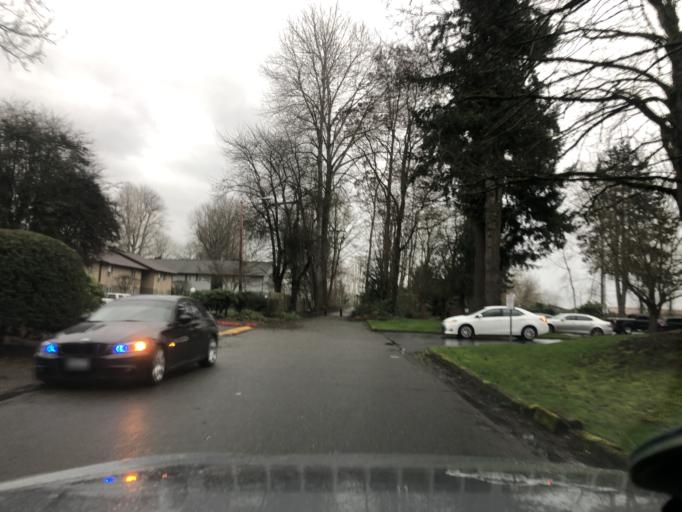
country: US
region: Washington
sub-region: King County
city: Kent
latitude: 47.3627
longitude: -122.2289
